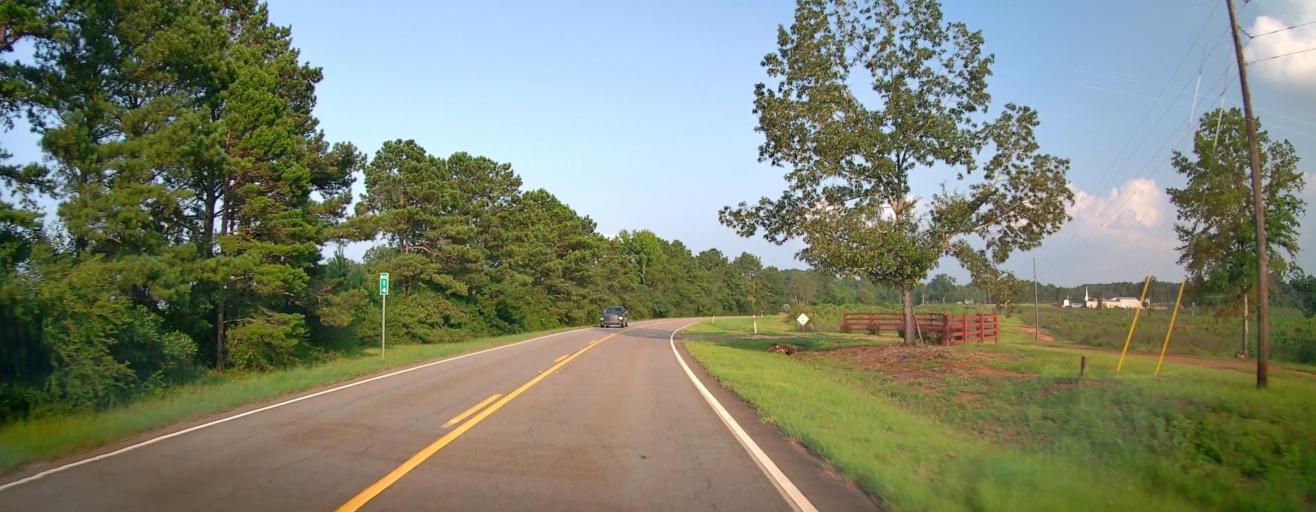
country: US
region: Georgia
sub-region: Jones County
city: Gray
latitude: 33.0589
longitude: -83.5636
